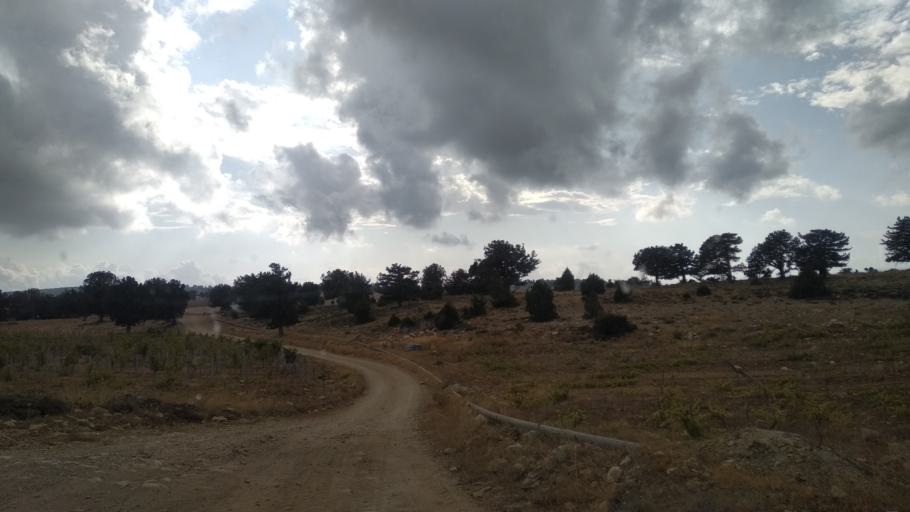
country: TR
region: Mersin
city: Sarikavak
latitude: 36.5676
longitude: 33.7417
